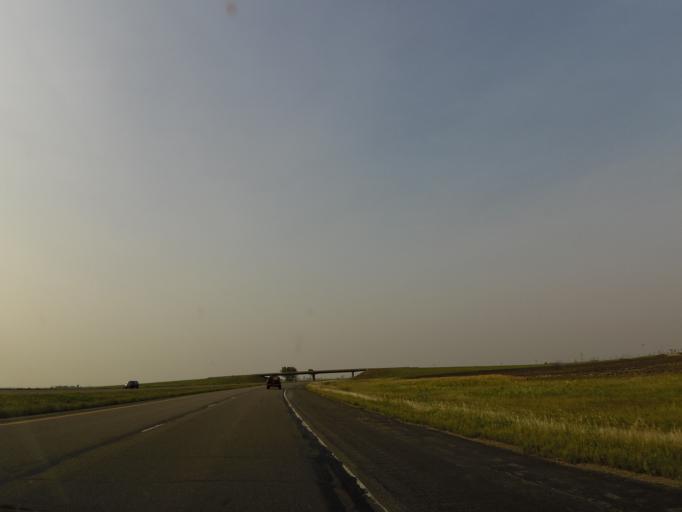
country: US
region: North Dakota
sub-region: Traill County
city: Hillsboro
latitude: 47.1919
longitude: -96.9893
